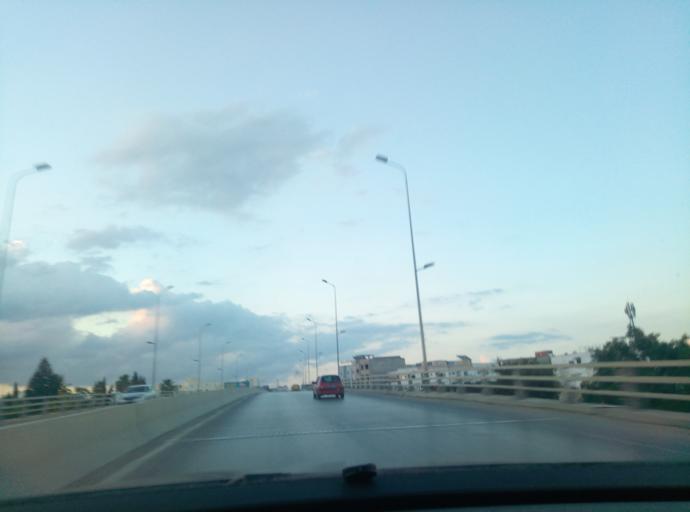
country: TN
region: Manouba
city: Manouba
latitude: 36.8020
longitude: 10.1190
